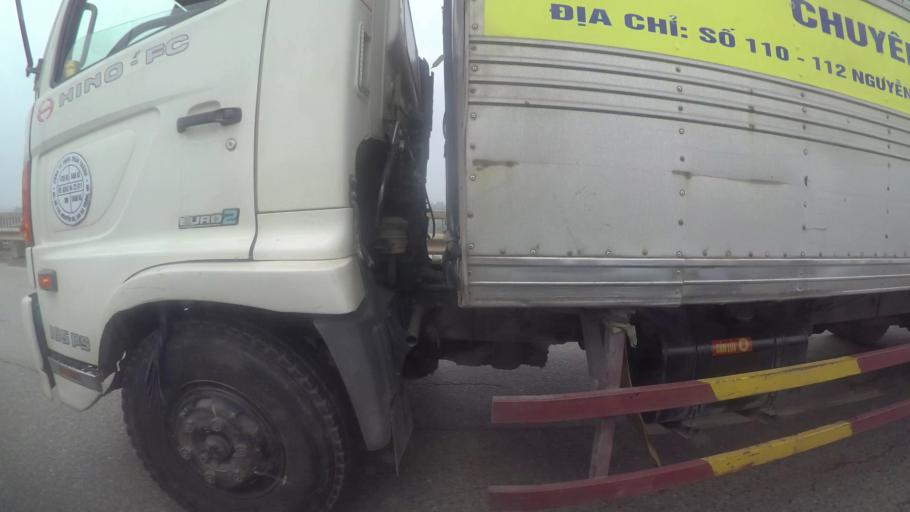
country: VN
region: Ha Noi
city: Tay Ho
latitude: 21.1004
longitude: 105.7866
